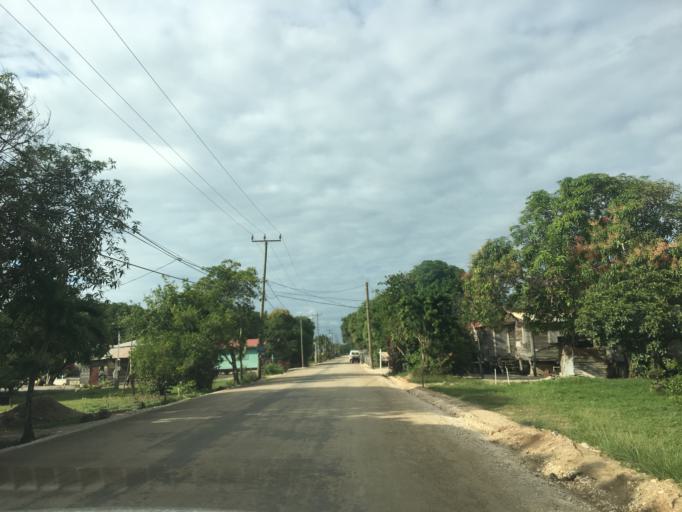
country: BZ
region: Stann Creek
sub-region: Dangriga
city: Dangriga
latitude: 16.8687
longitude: -88.2866
